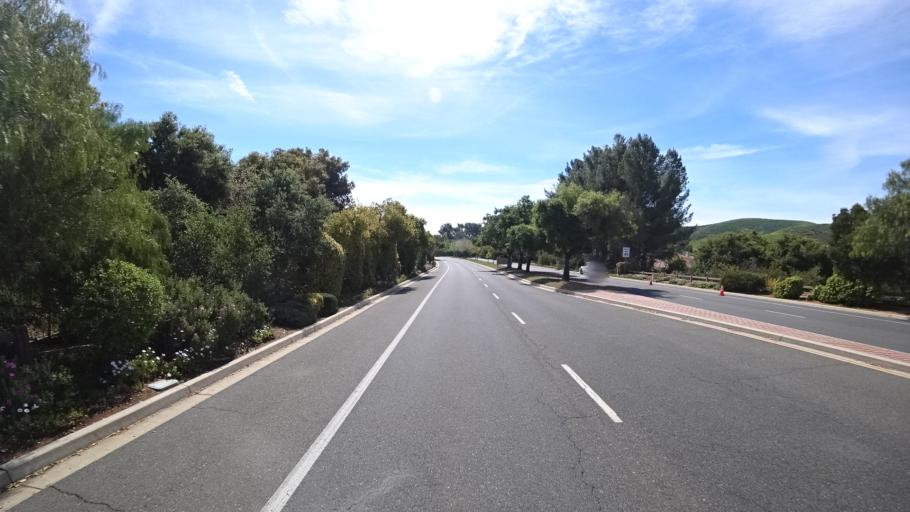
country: US
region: California
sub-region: Ventura County
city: Oak Park
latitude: 34.1944
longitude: -118.8020
